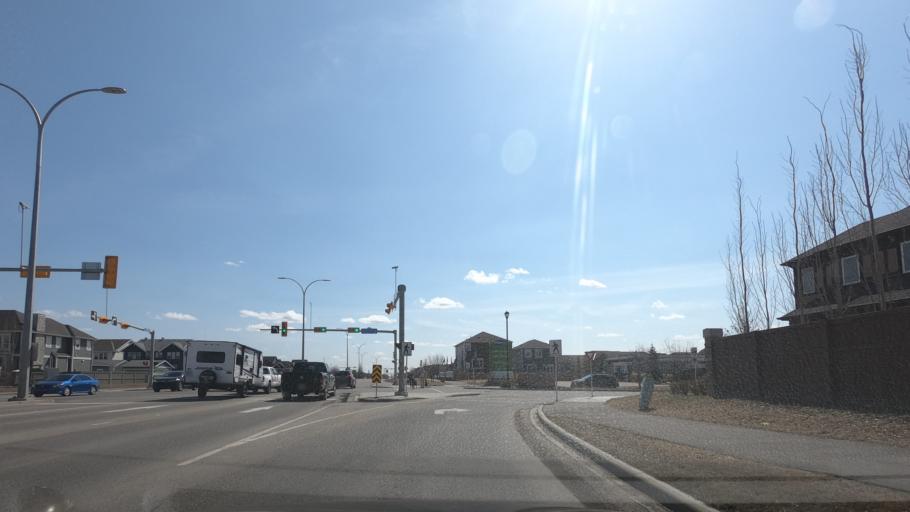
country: CA
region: Alberta
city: Airdrie
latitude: 51.2607
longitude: -114.0254
